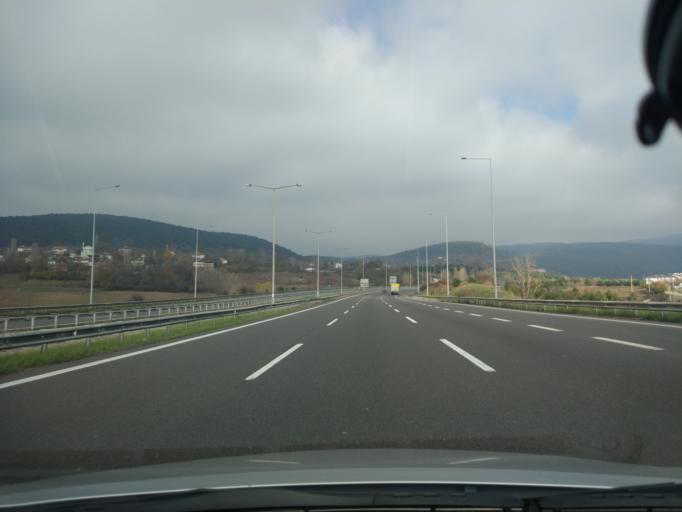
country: TR
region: Bolu
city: Bolu
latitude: 40.7455
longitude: 31.5614
